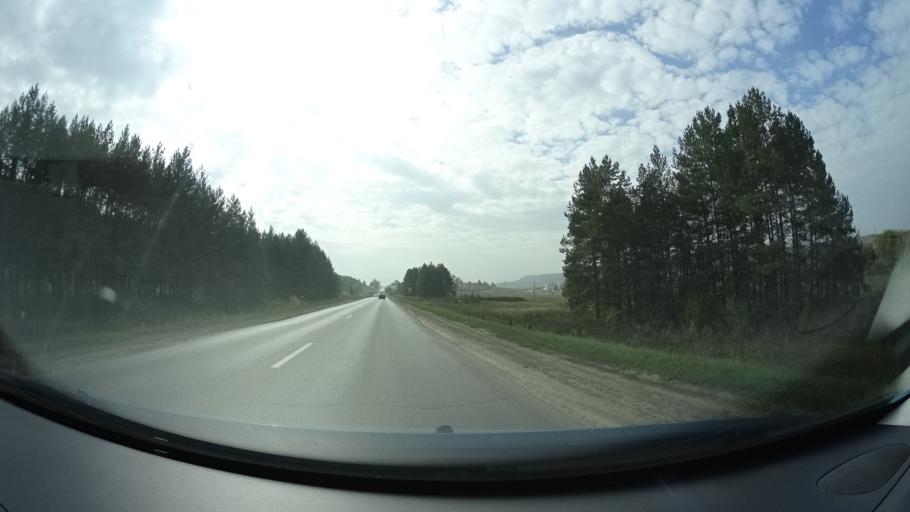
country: RU
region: Bashkortostan
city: Oktyabr'skiy
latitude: 54.5252
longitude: 53.5468
